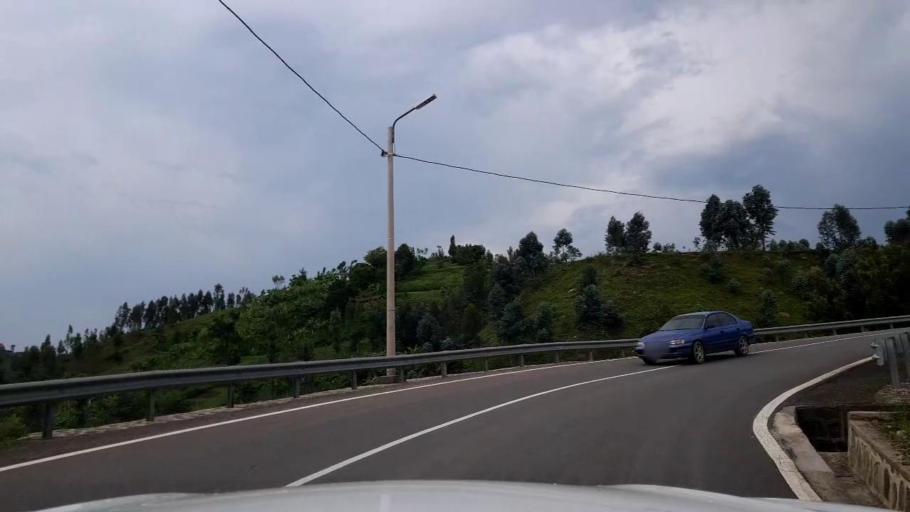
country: RW
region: Western Province
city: Kibuye
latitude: -2.0323
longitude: 29.3974
